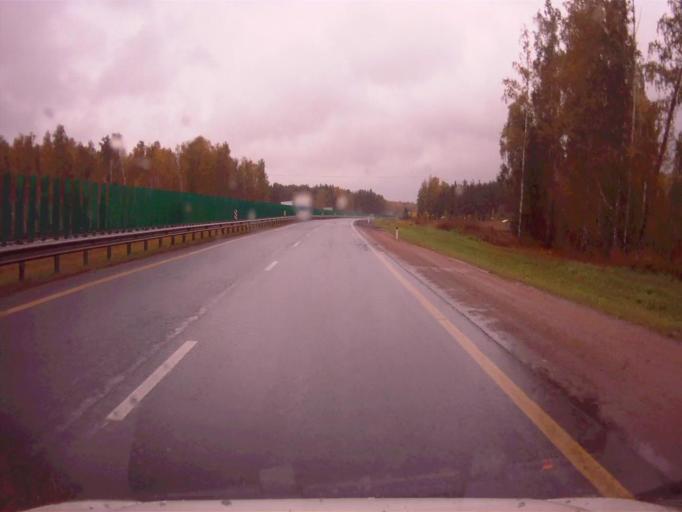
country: RU
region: Chelyabinsk
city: Dolgoderevenskoye
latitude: 55.3365
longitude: 61.3100
